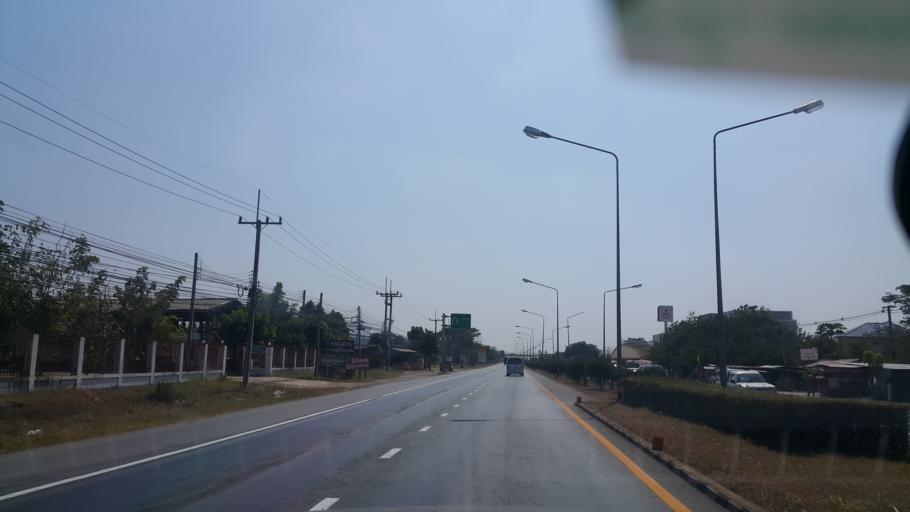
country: TH
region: Khon Kaen
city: Phon
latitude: 15.8226
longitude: 102.6078
